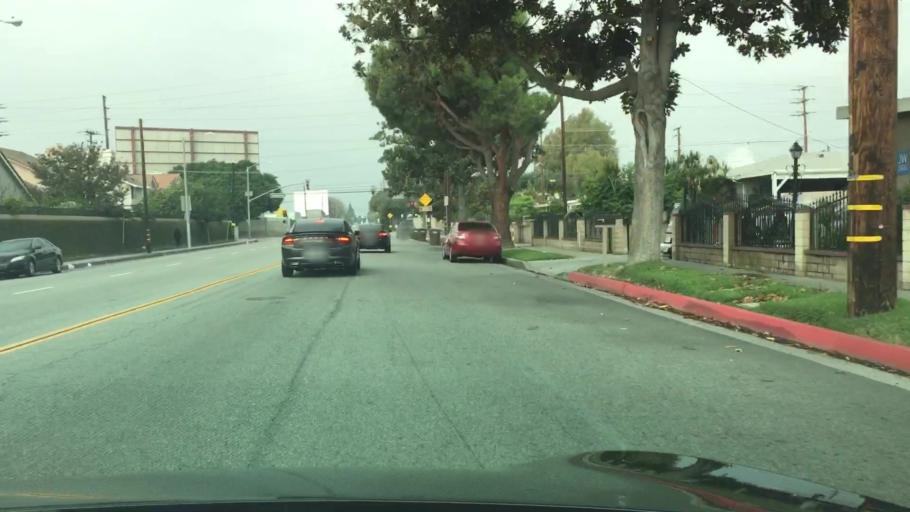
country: US
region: California
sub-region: Los Angeles County
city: West Puente Valley
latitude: 34.0532
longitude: -117.9857
